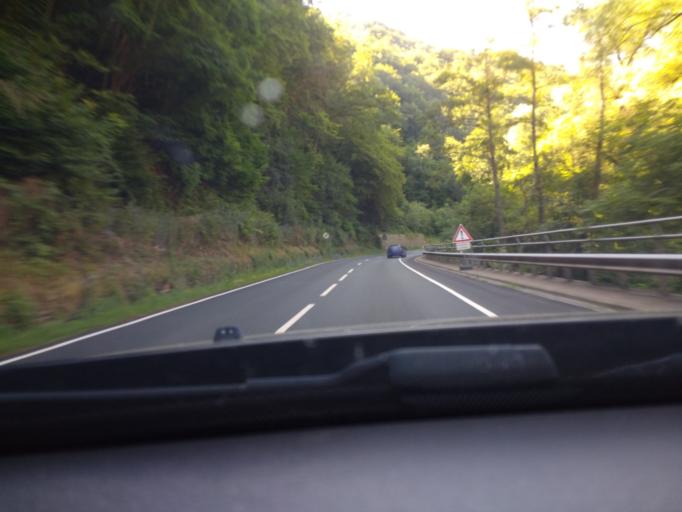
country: DE
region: Rheinland-Pfalz
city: Alf
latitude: 50.0564
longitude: 7.1042
